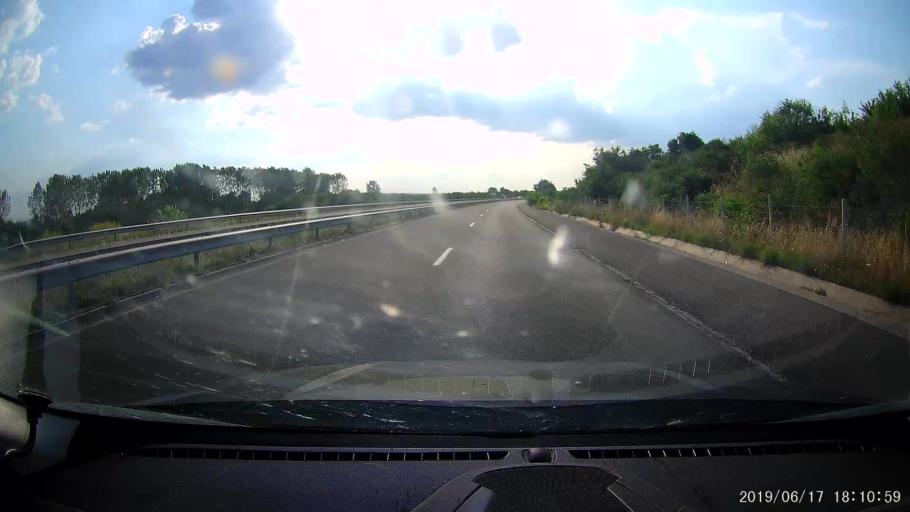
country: BG
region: Khaskovo
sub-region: Obshtina Lyubimets
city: Lyubimets
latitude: 41.8781
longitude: 26.0624
